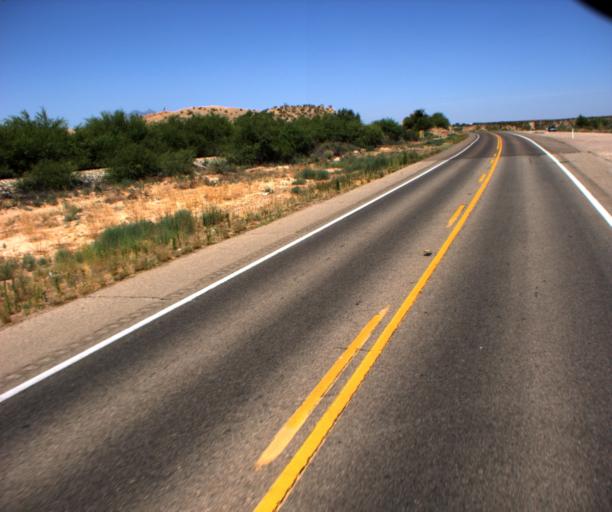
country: US
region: Arizona
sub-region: Graham County
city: Bylas
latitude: 33.0716
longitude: -110.0197
